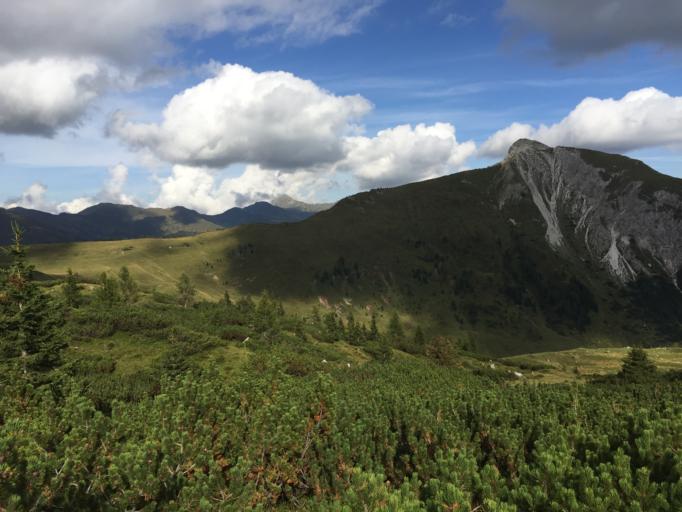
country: IT
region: Veneto
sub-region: Provincia di Belluno
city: San Pietro di Cadore
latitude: 46.6194
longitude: 12.5732
